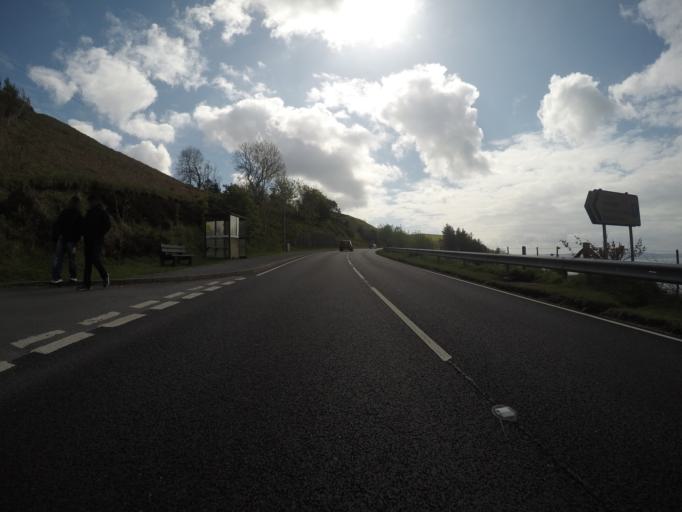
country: GB
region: Scotland
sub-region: Highland
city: Portree
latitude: 57.5841
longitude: -6.3573
